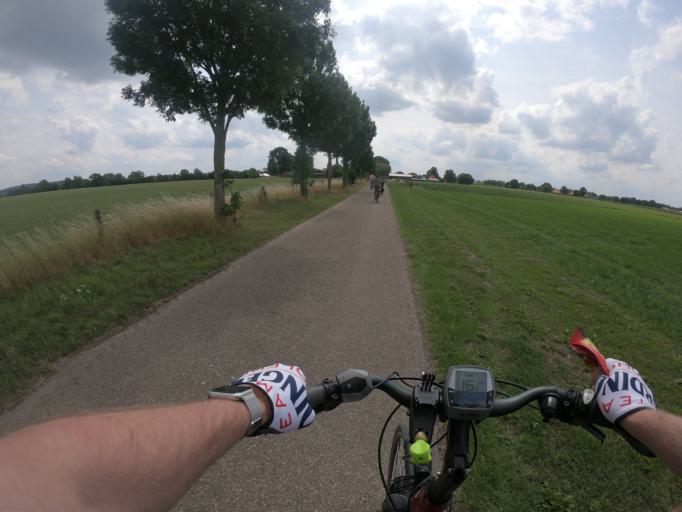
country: NL
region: Gelderland
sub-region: Gemeente Groesbeek
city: De Horst
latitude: 51.7859
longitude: 5.9635
